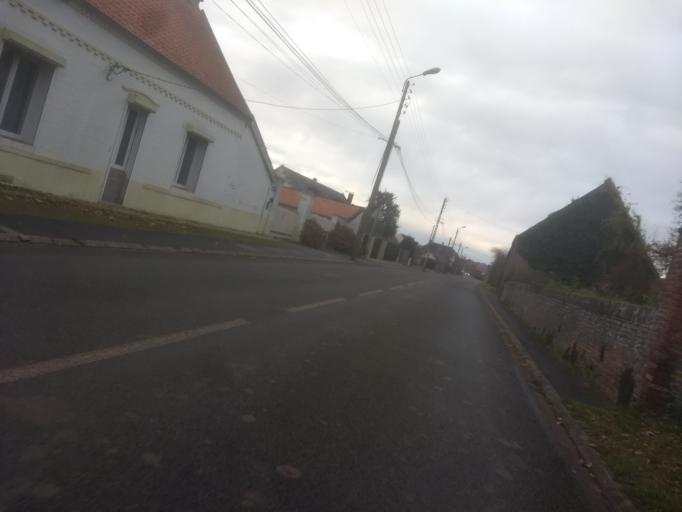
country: FR
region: Nord-Pas-de-Calais
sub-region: Departement du Pas-de-Calais
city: Riviere
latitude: 50.2357
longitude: 2.7012
